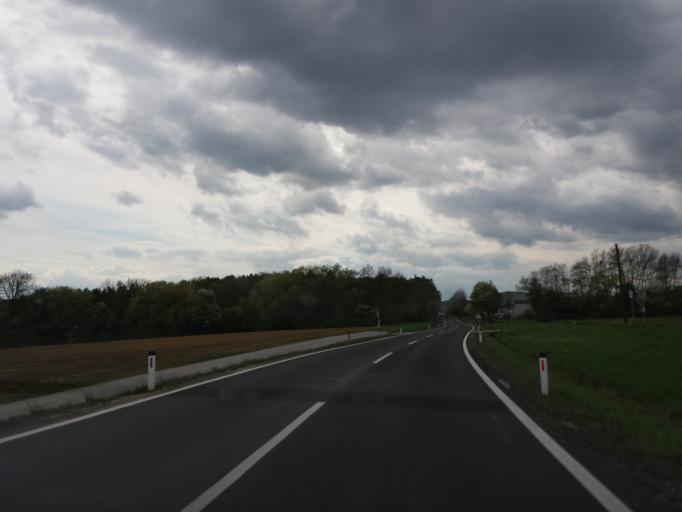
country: AT
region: Styria
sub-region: Politischer Bezirk Hartberg-Fuerstenfeld
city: Fuerstenfeld
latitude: 47.0275
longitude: 16.0775
